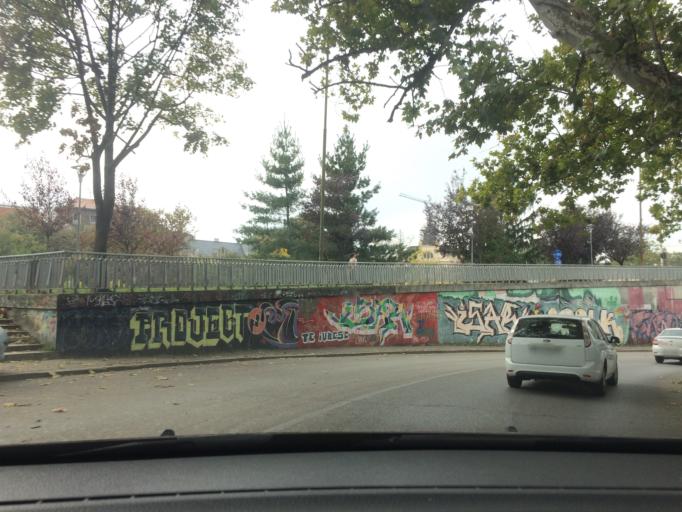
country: RO
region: Timis
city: Timisoara
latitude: 45.7500
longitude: 21.2225
